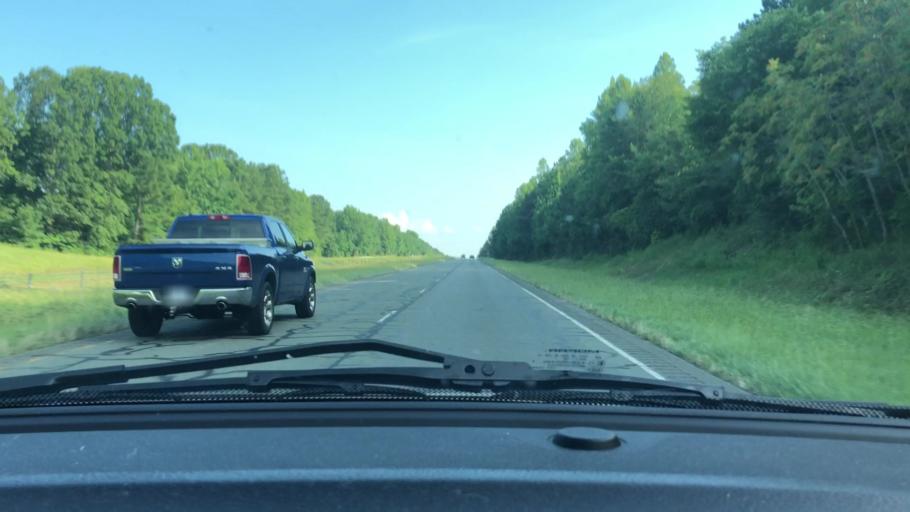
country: US
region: North Carolina
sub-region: Chatham County
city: Siler City
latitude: 35.7192
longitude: -79.4299
